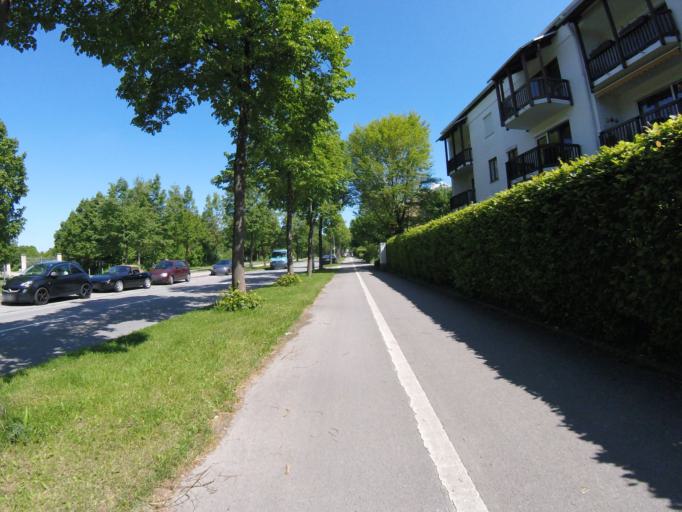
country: DE
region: Bavaria
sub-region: Upper Bavaria
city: Unterhaching
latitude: 48.0966
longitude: 11.6257
